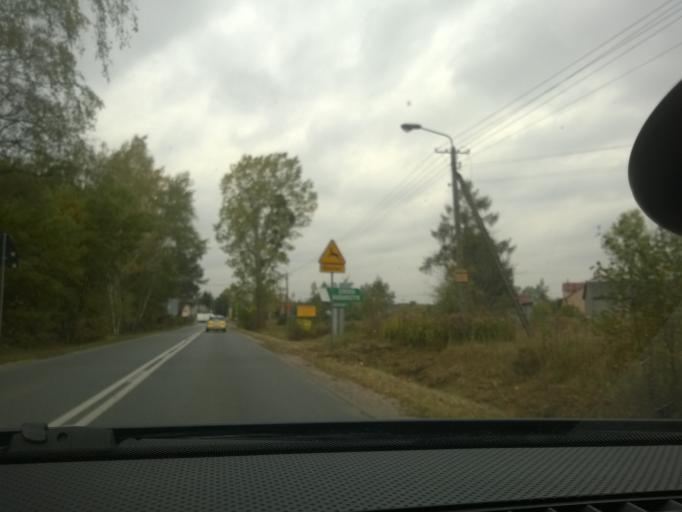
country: PL
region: Masovian Voivodeship
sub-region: Powiat pruszkowski
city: Granica
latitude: 52.1204
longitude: 20.7967
